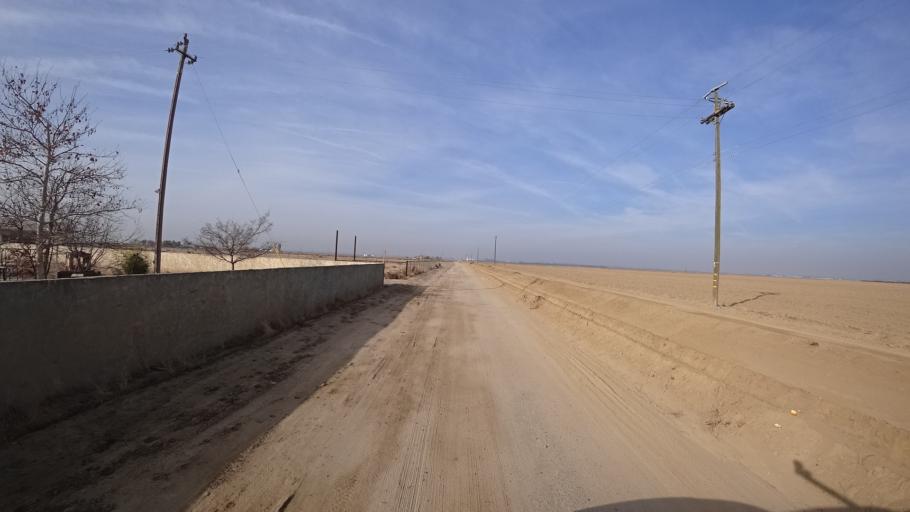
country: US
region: California
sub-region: Kern County
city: Lamont
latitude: 35.3251
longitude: -118.9420
